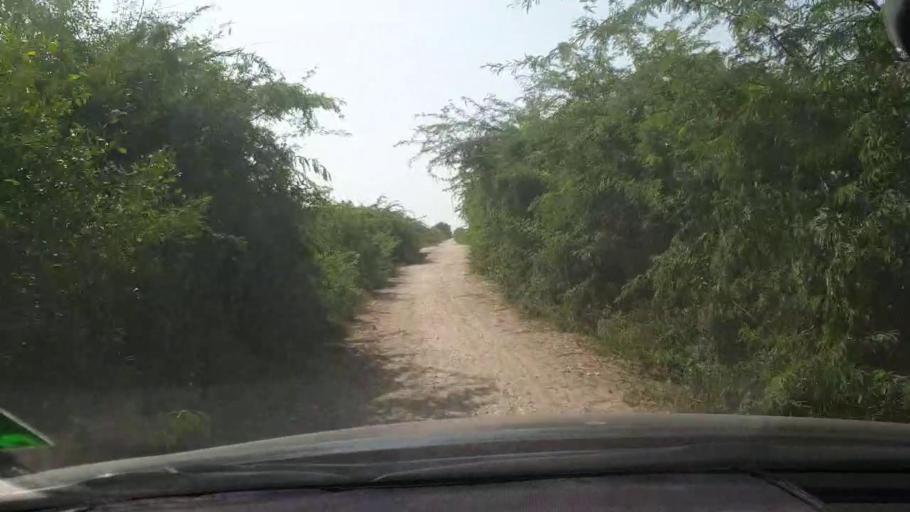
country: PK
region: Sindh
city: Naukot
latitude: 24.7959
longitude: 69.2452
